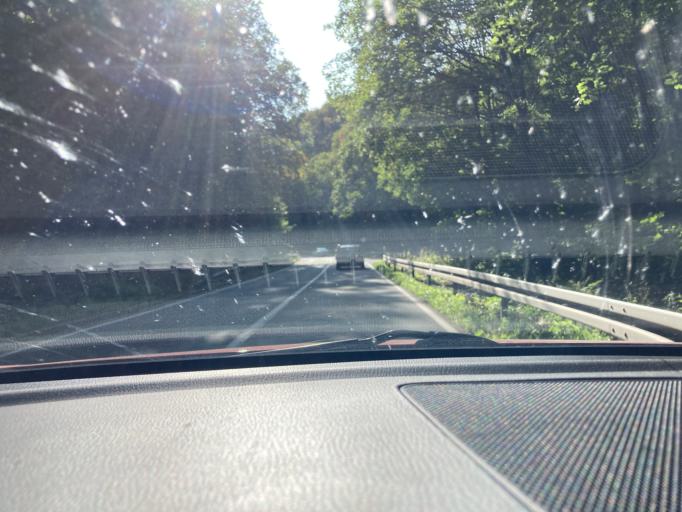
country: DE
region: Saxony-Anhalt
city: Thale
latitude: 51.7320
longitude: 11.0309
